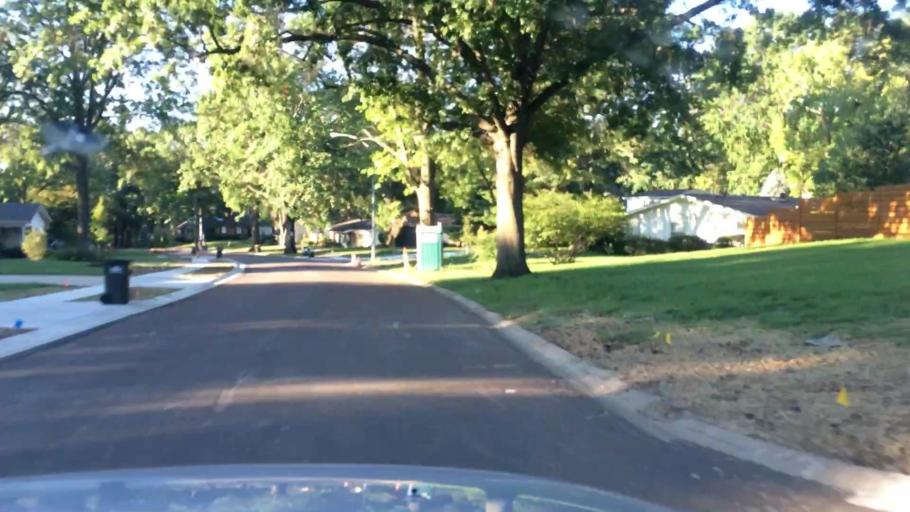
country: US
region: Kansas
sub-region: Johnson County
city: Overland Park
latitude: 38.9694
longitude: -94.6529
